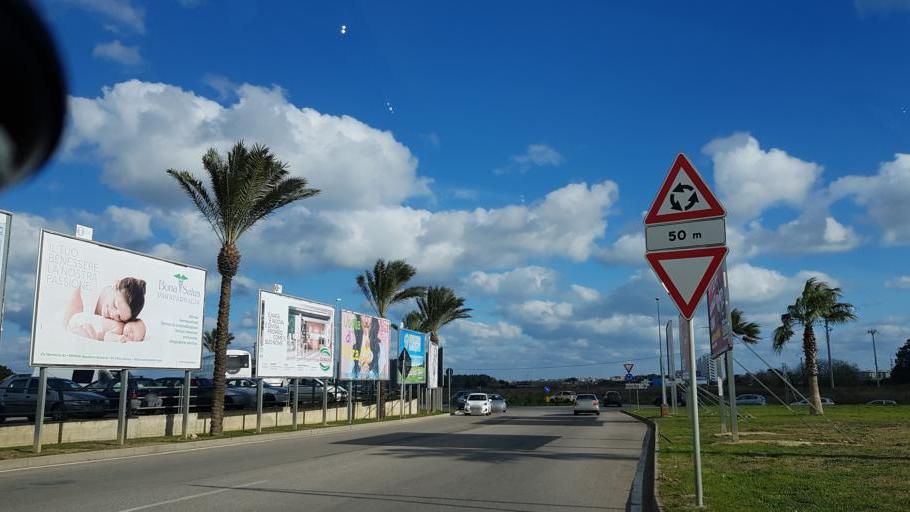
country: IT
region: Apulia
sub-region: Provincia di Brindisi
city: Brindisi
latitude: 40.6189
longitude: 17.9039
